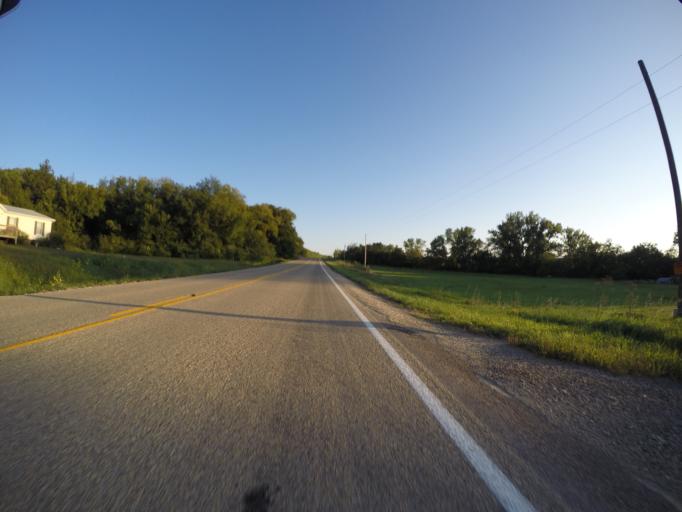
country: US
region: Kansas
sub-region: Riley County
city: Manhattan
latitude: 39.1487
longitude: -96.5579
